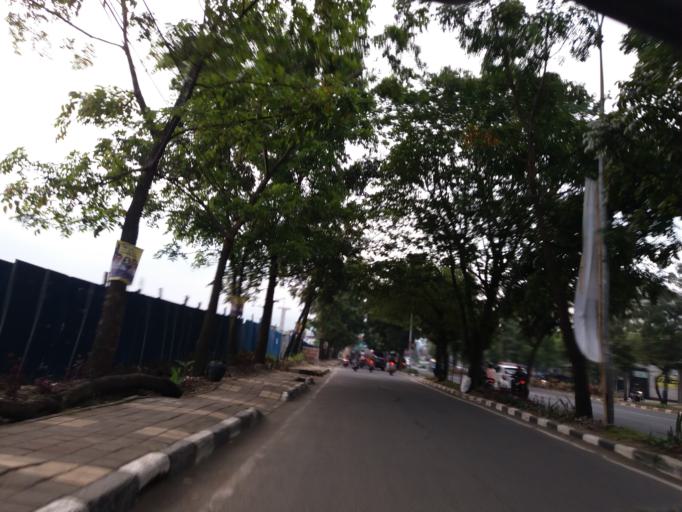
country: ID
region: West Java
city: Bandung
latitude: -6.9162
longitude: 107.6438
